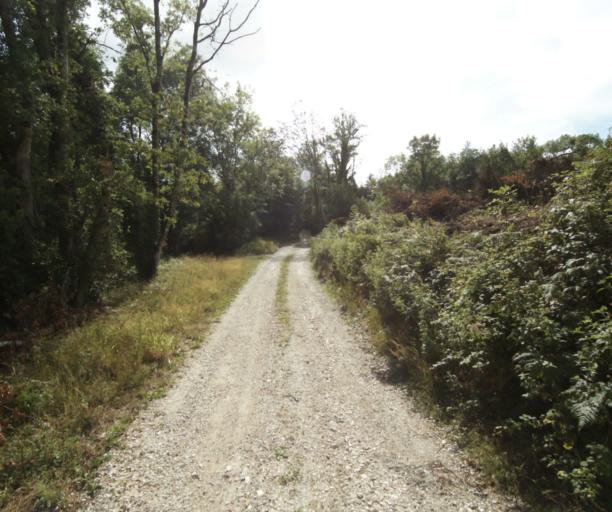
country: FR
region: Midi-Pyrenees
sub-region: Departement du Tarn
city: Dourgne
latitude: 43.4587
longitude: 2.1190
